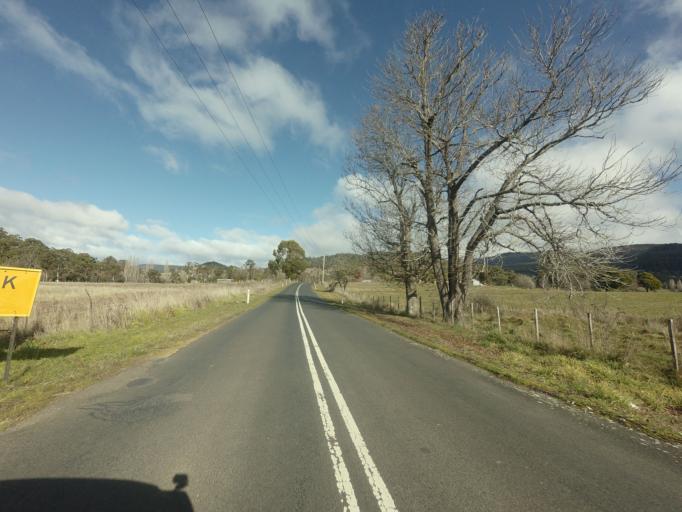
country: AU
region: Tasmania
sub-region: Derwent Valley
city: New Norfolk
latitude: -42.6005
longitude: 146.7068
